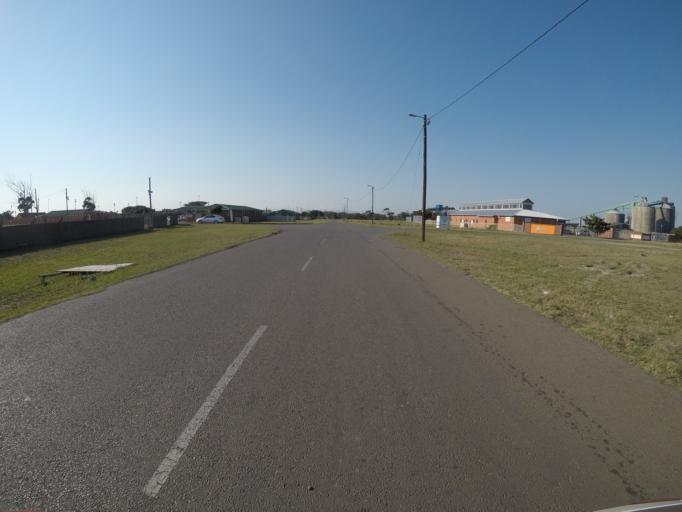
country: ZA
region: KwaZulu-Natal
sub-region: uThungulu District Municipality
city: Richards Bay
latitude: -28.7570
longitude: 32.0329
